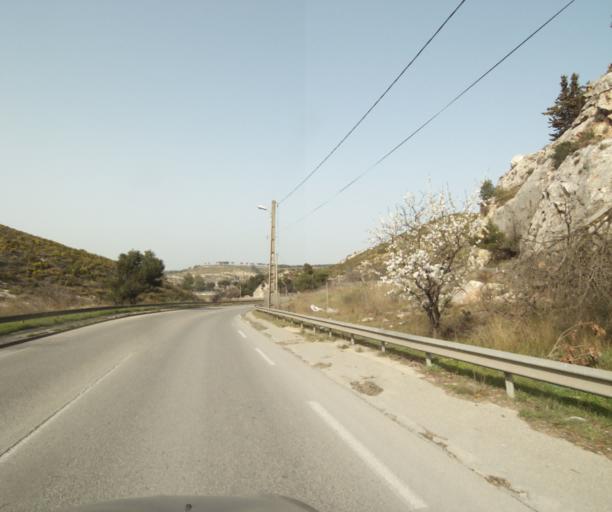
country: FR
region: Provence-Alpes-Cote d'Azur
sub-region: Departement des Bouches-du-Rhone
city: Les Pennes-Mirabeau
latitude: 43.4035
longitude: 5.3325
